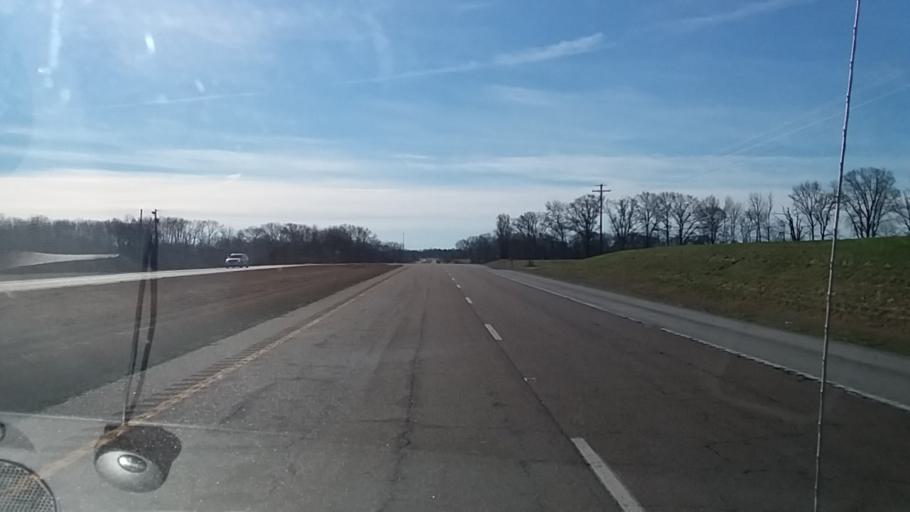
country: US
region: Tennessee
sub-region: Lauderdale County
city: Halls
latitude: 35.9318
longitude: -89.2881
